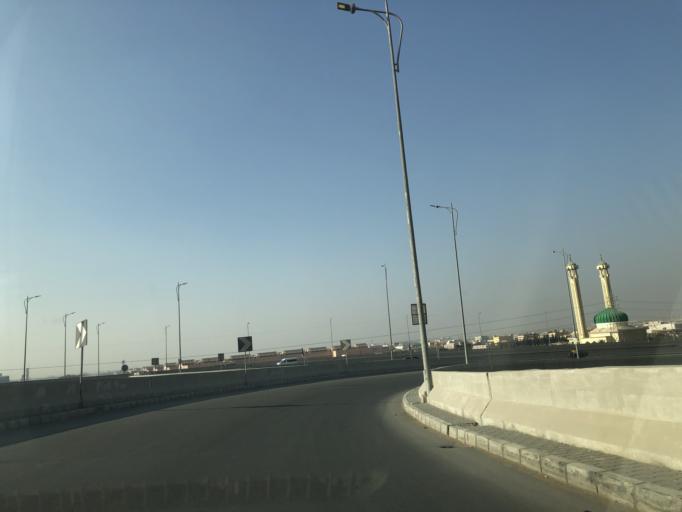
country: EG
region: Al Jizah
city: Madinat Sittah Uktubar
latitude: 29.8933
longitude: 30.8955
